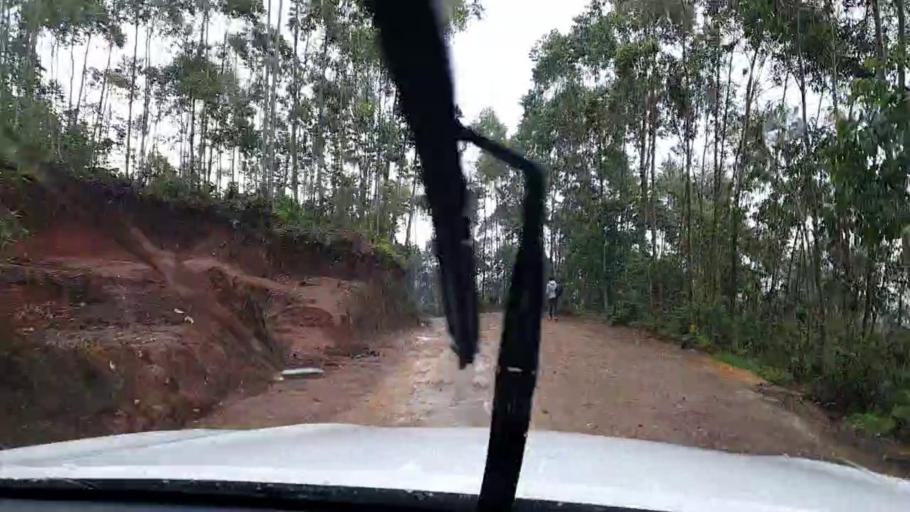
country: RW
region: Western Province
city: Cyangugu
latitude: -2.5484
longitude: 28.9788
